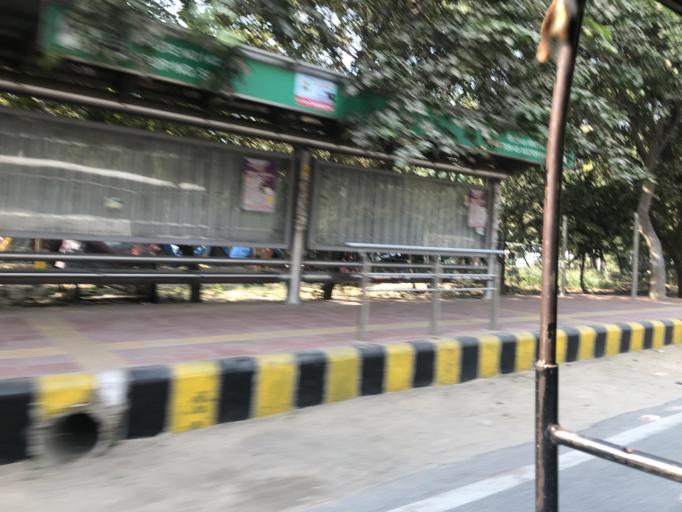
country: IN
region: Haryana
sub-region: Gurgaon
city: Gurgaon
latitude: 28.4512
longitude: 77.0764
